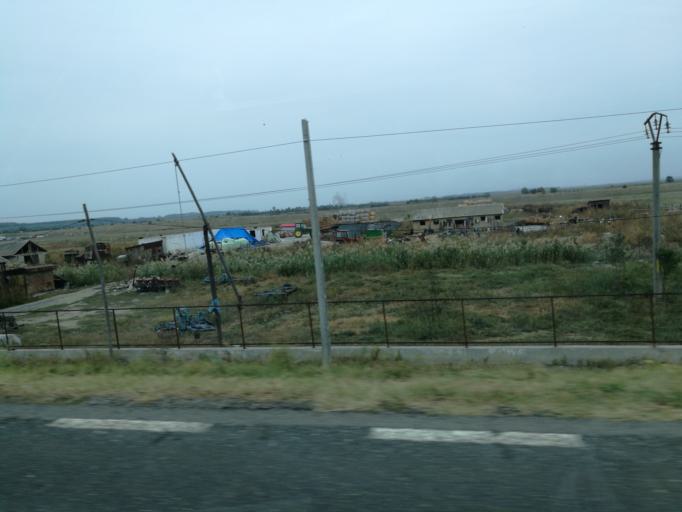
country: RO
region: Braila
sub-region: Municipiul Braila
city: Braila
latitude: 45.2833
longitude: 28.0101
